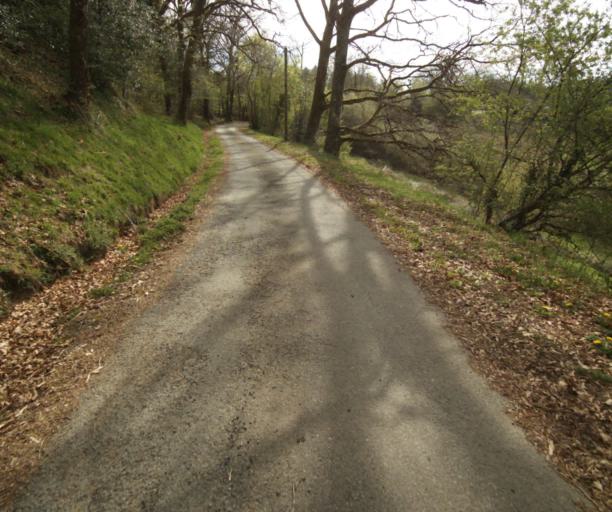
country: FR
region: Limousin
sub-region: Departement de la Correze
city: Correze
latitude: 45.3851
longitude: 1.8188
